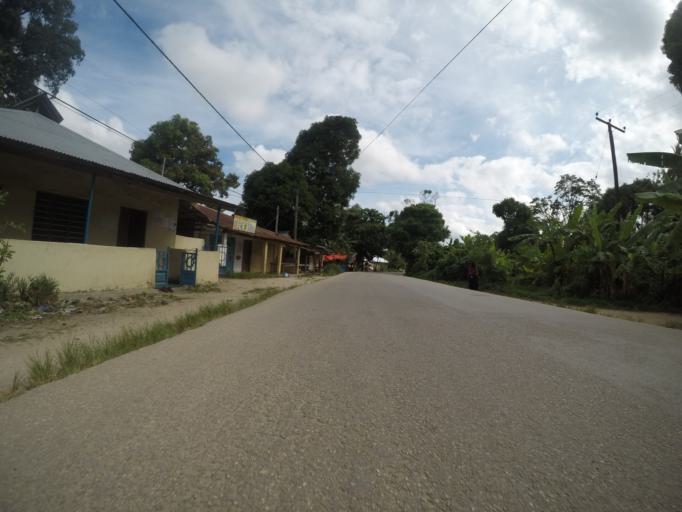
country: TZ
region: Pemba South
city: Chake Chake
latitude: -5.2416
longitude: 39.7821
